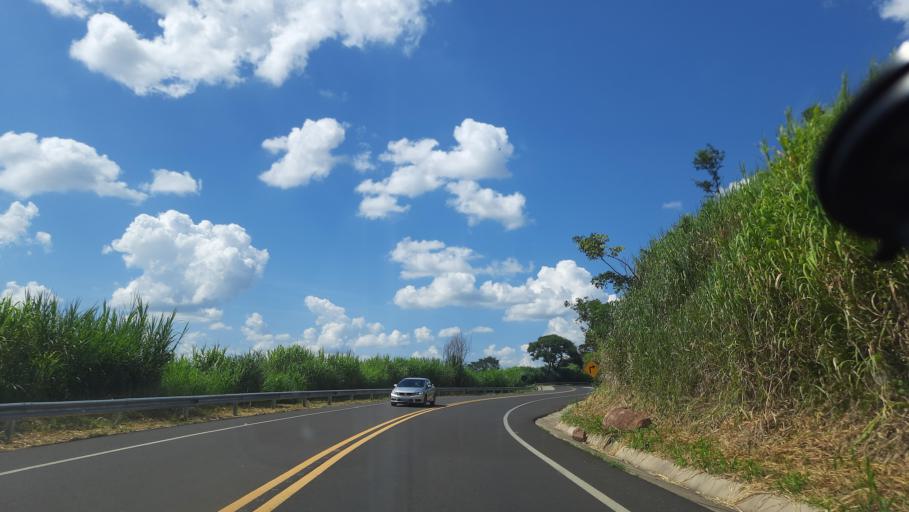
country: BR
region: Sao Paulo
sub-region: Sao Jose Do Rio Pardo
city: Sao Jose do Rio Pardo
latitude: -21.5997
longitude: -46.9380
